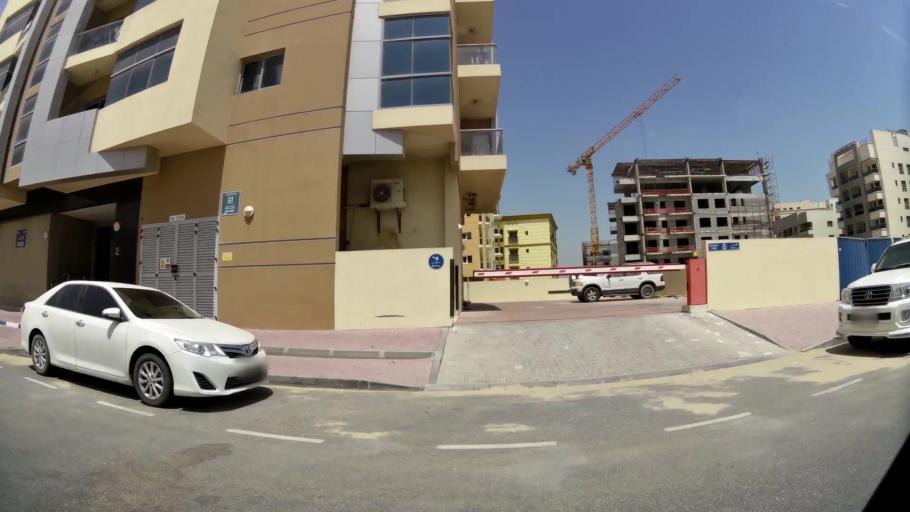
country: AE
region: Ash Shariqah
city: Sharjah
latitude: 25.1833
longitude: 55.4036
